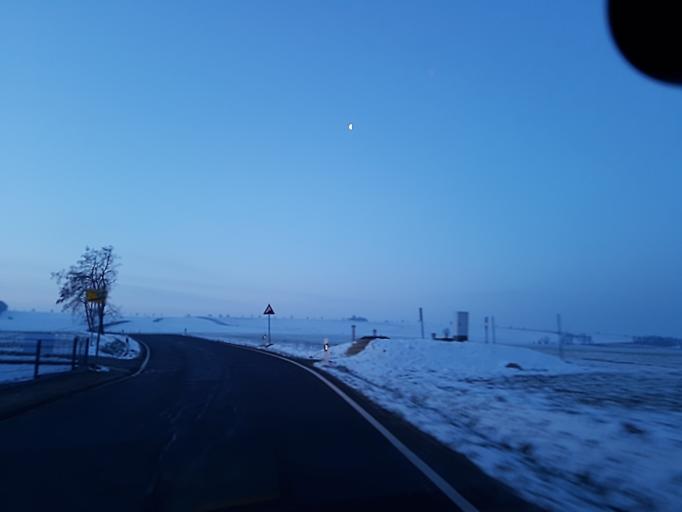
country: DE
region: Saxony
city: Cavertitz
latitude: 51.3629
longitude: 13.1421
